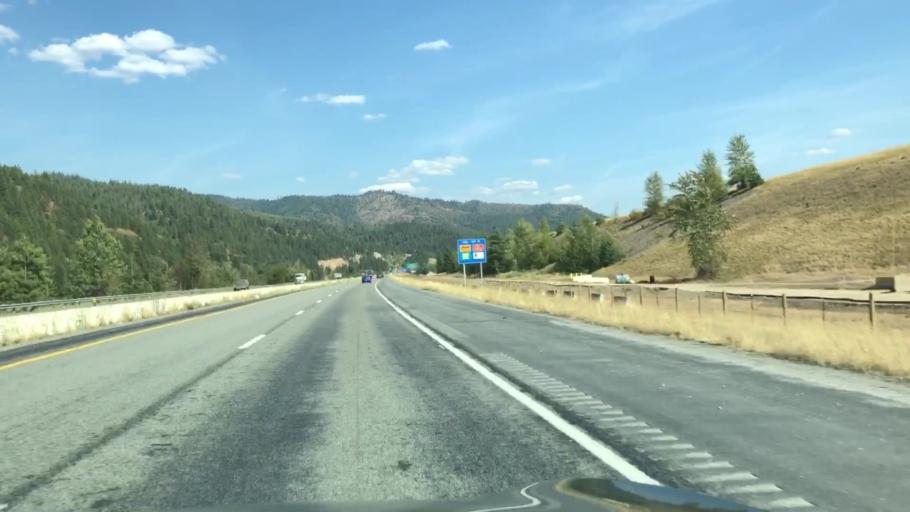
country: US
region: Idaho
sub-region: Shoshone County
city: Kellogg
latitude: 47.5480
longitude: -116.1588
